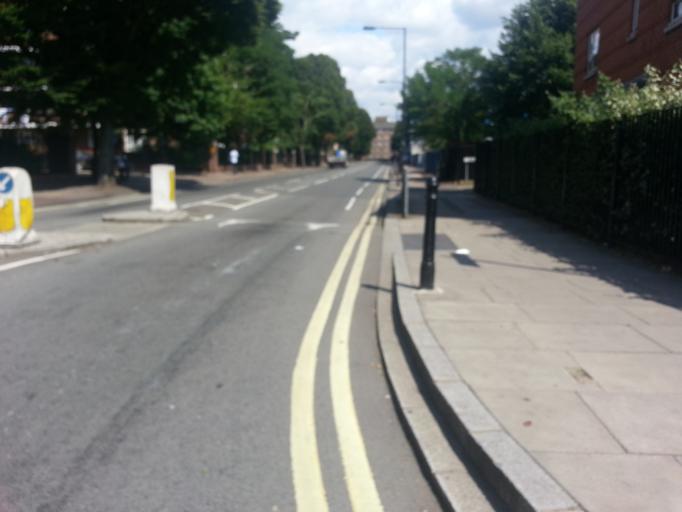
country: GB
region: England
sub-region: Greater London
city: Hammersmith
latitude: 51.5099
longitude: -0.2345
